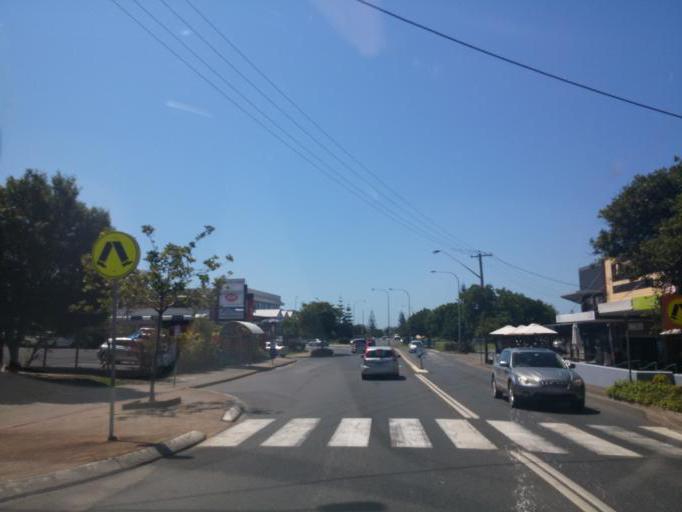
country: AU
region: New South Wales
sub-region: Coffs Harbour
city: Coffs Harbour
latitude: -30.3039
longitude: 153.1369
